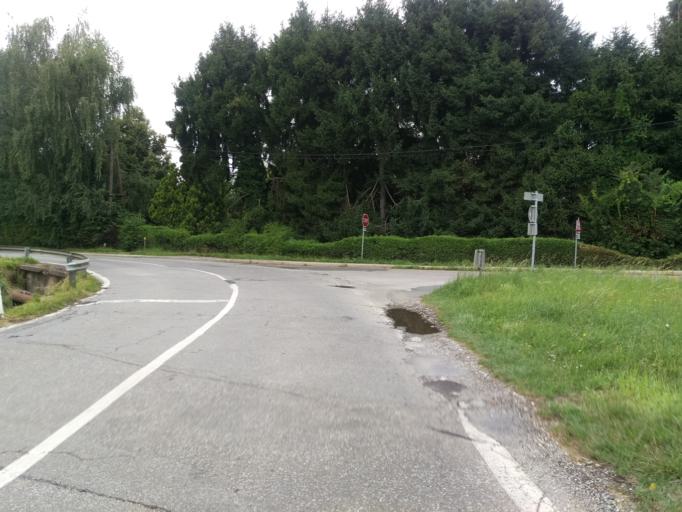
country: AT
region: Styria
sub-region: Politischer Bezirk Graz-Umgebung
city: Hart bei Graz
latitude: 47.0404
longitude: 15.5064
